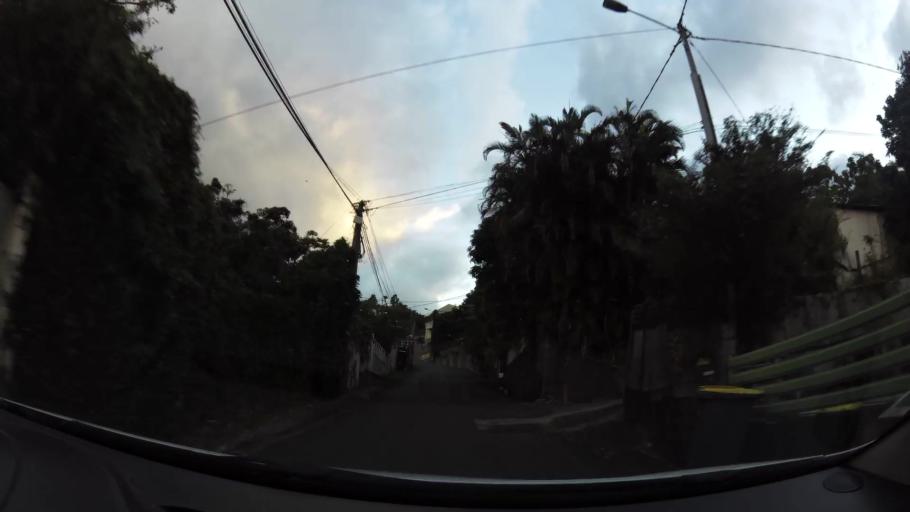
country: RE
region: Reunion
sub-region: Reunion
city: Saint-Denis
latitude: -20.9129
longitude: 55.4595
